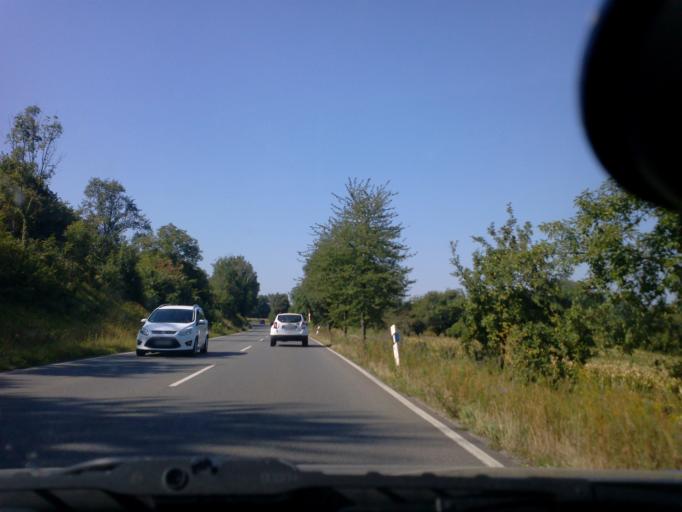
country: DE
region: Baden-Wuerttemberg
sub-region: Karlsruhe Region
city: Weingarten
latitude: 49.0780
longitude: 8.5469
